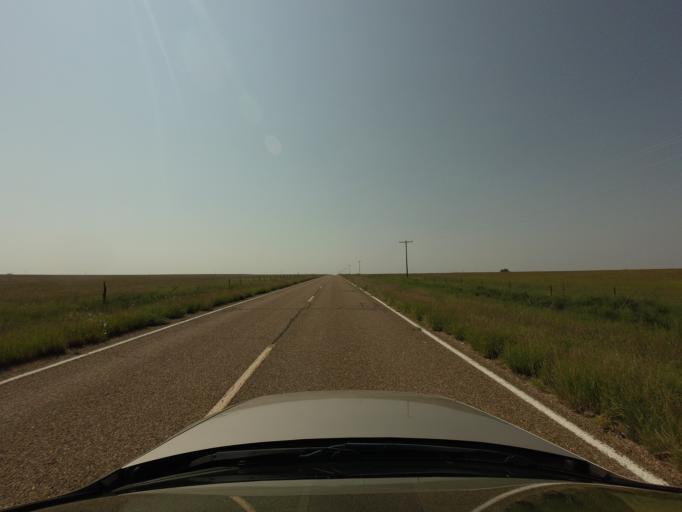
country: US
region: New Mexico
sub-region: Curry County
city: Cannon Air Force Base
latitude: 34.6810
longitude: -103.6355
